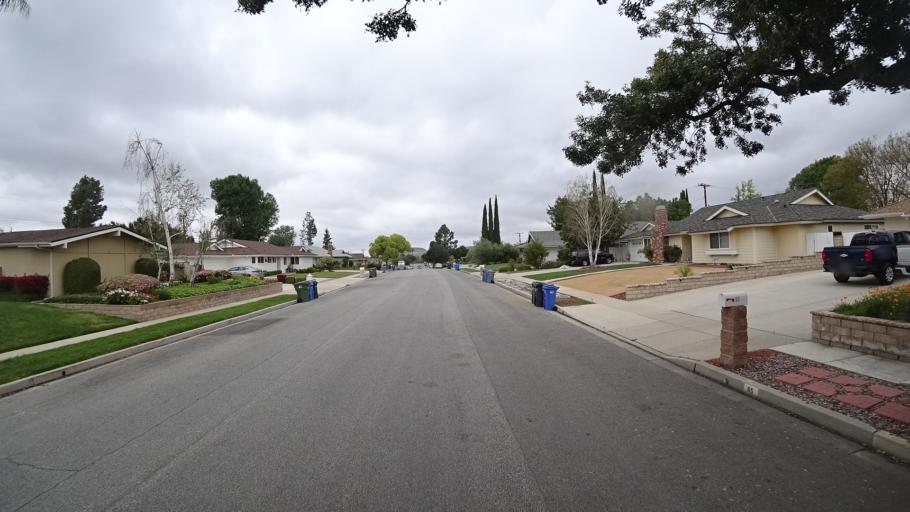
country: US
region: California
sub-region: Ventura County
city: Thousand Oaks
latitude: 34.2084
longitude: -118.8742
